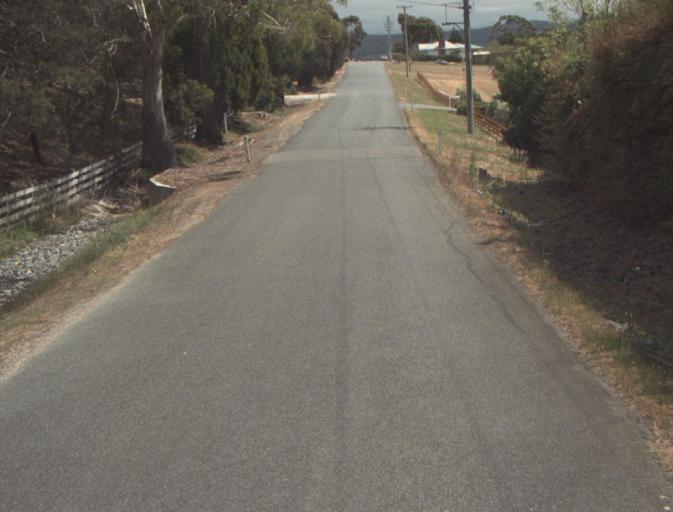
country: AU
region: Tasmania
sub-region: Launceston
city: Newstead
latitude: -41.4497
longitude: 147.2081
